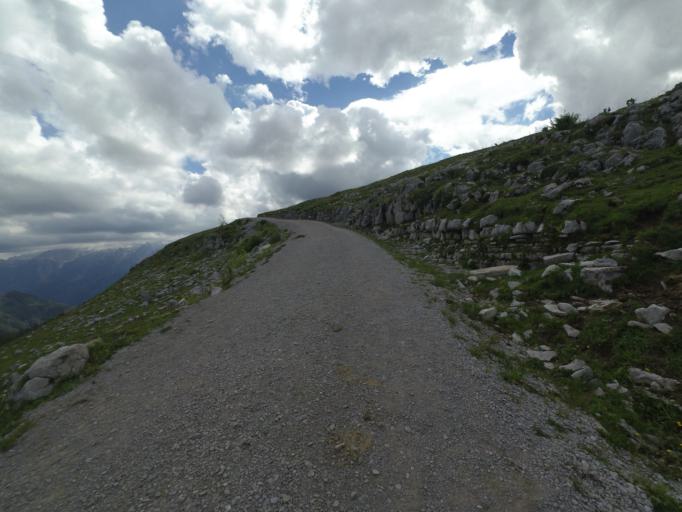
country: AT
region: Salzburg
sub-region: Politischer Bezirk Salzburg-Umgebung
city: Hintersee
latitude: 47.6559
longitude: 13.2938
